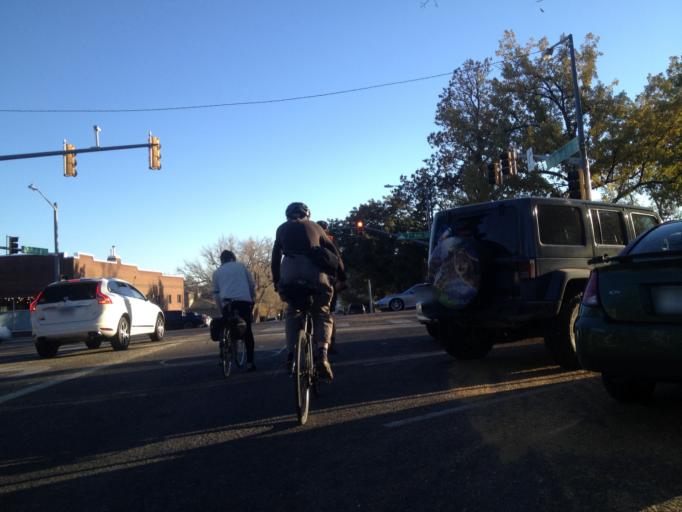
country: US
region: Colorado
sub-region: Boulder County
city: Longmont
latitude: 40.1643
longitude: -105.1039
